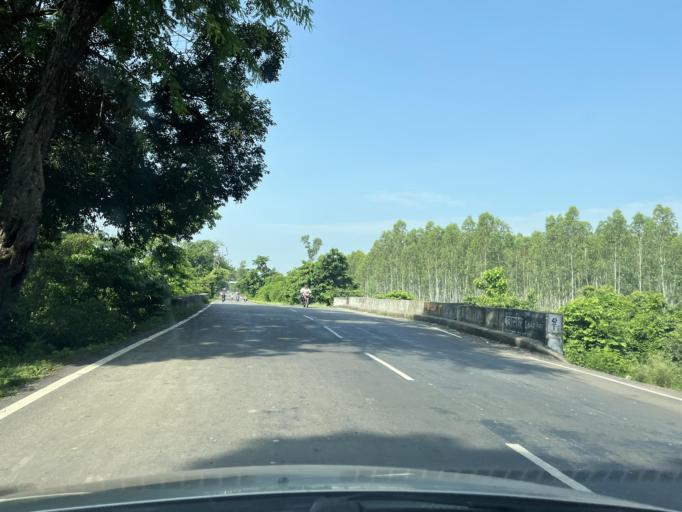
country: IN
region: Uttarakhand
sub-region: Udham Singh Nagar
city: Bazpur
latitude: 29.2171
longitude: 79.2281
